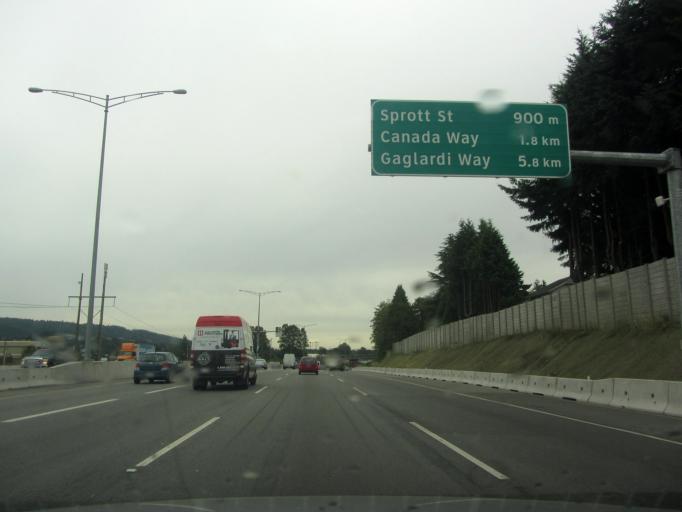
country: CA
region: British Columbia
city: Burnaby
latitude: 49.2586
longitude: -123.0202
